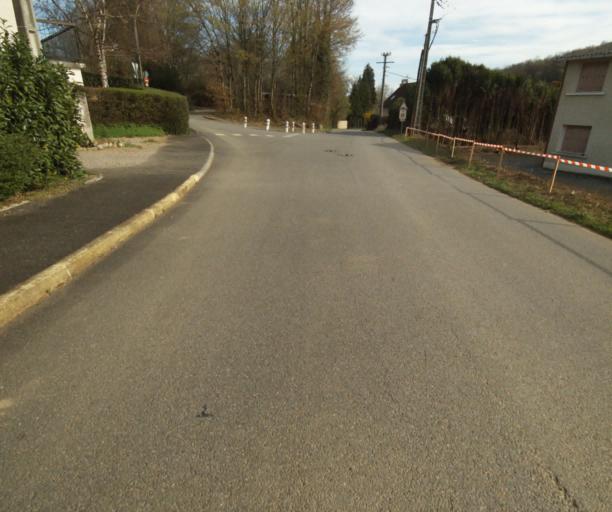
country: FR
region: Limousin
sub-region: Departement de la Correze
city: Tulle
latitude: 45.2881
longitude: 1.7648
